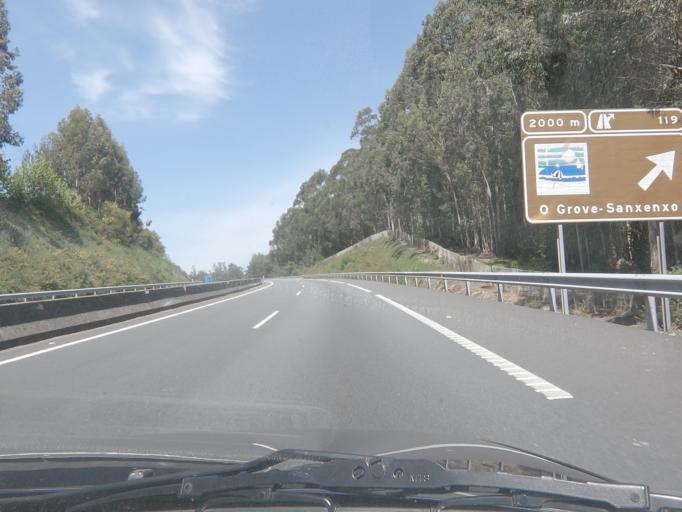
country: ES
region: Galicia
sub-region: Provincia de Pontevedra
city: Barro
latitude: 42.4998
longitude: -8.6520
